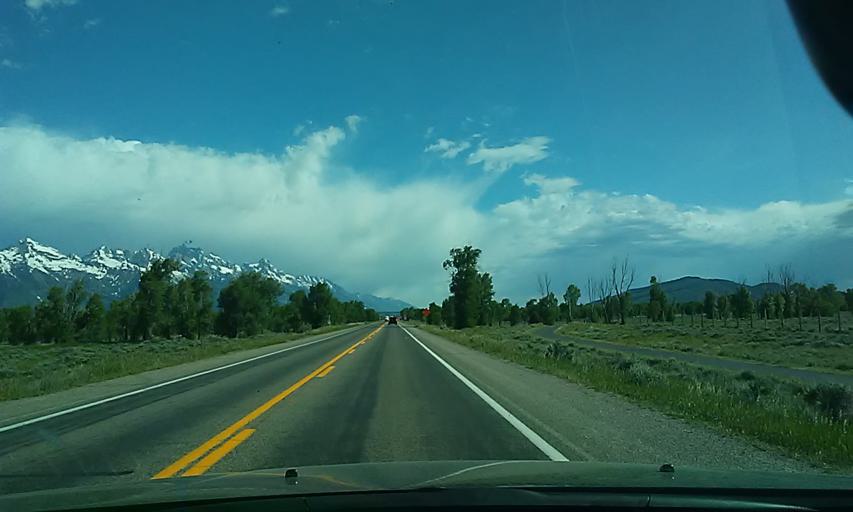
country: US
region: Wyoming
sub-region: Teton County
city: Jackson
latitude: 43.5608
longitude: -110.7330
